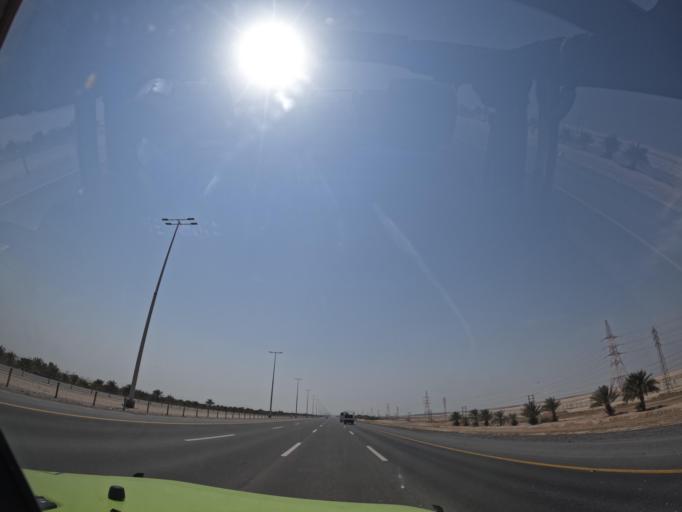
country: AE
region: Abu Dhabi
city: Abu Dhabi
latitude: 24.1987
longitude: 54.3950
